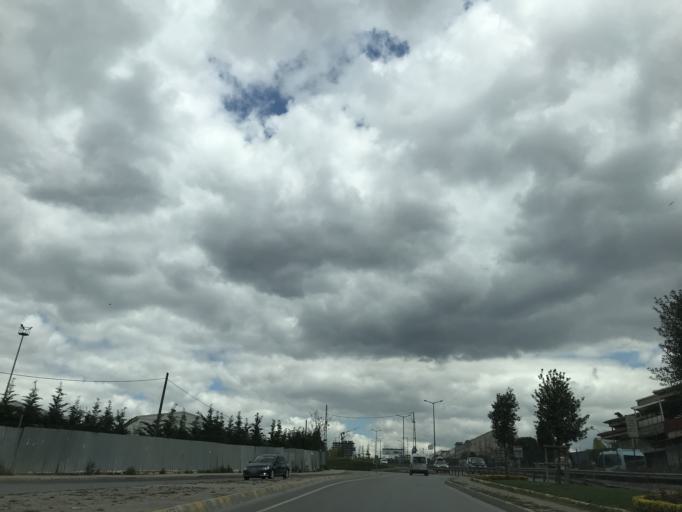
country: TR
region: Istanbul
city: Maltepe
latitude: 40.9010
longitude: 29.2067
